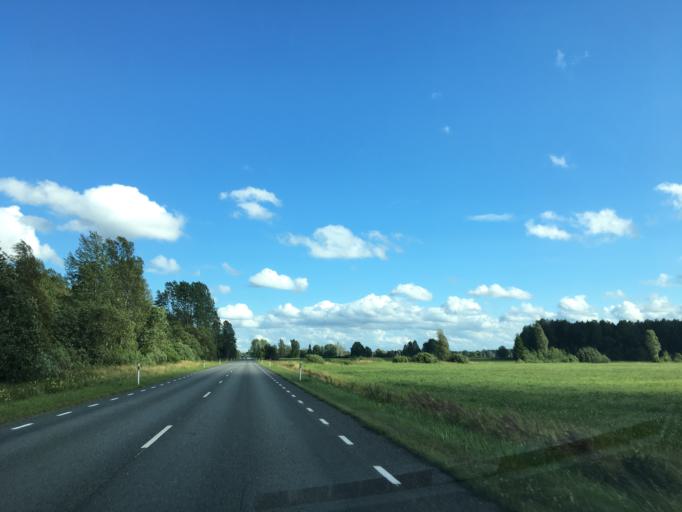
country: EE
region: Paernumaa
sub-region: Vaendra vald (alev)
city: Vandra
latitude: 58.5896
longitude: 25.1633
